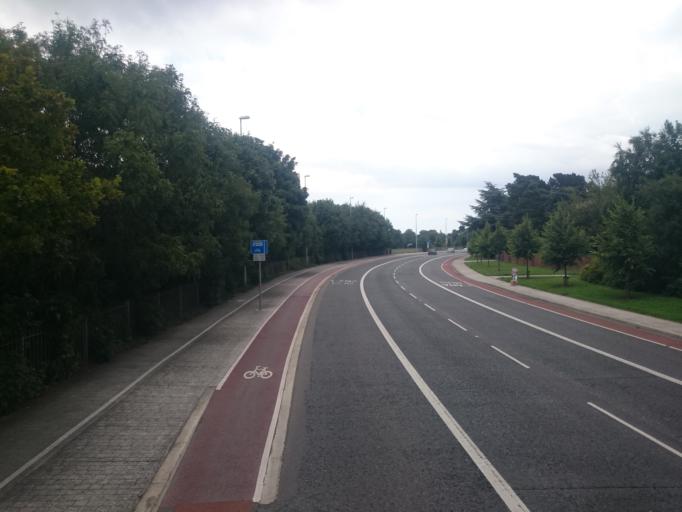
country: IE
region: Leinster
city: Ballyboden
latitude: 53.2892
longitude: -6.3233
